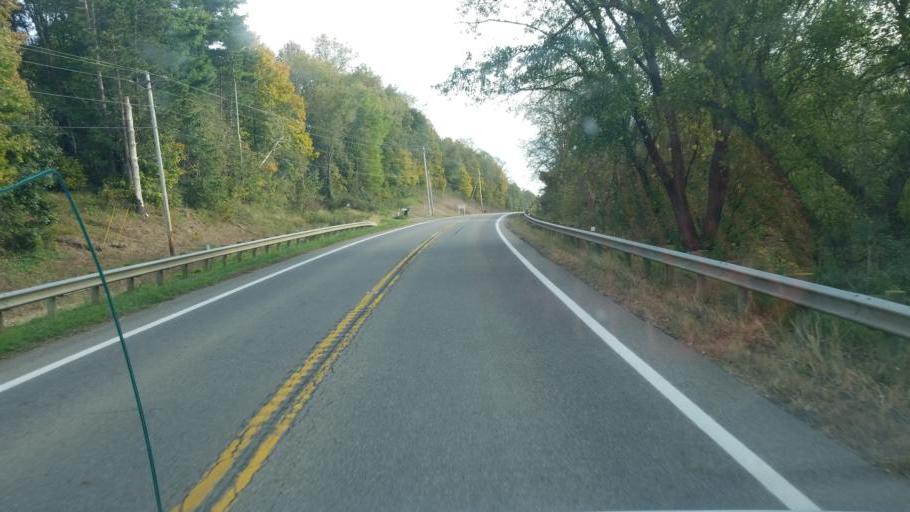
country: US
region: Ohio
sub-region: Wayne County
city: Shreve
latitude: 40.6647
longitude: -81.9439
